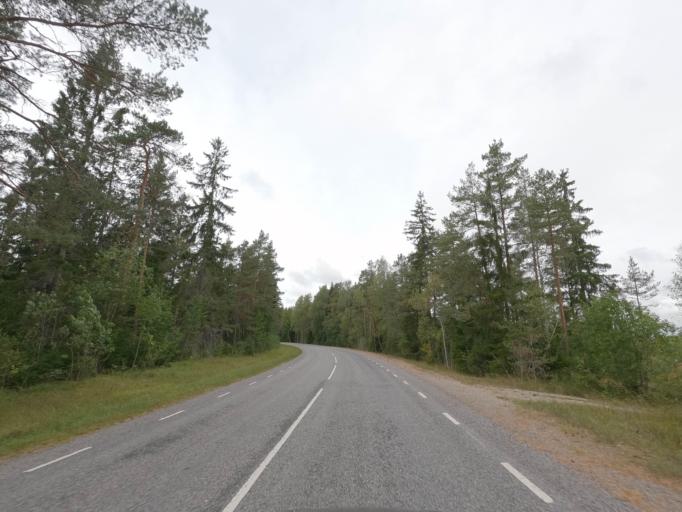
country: EE
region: Raplamaa
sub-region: Rapla vald
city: Rapla
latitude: 59.0096
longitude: 24.6054
